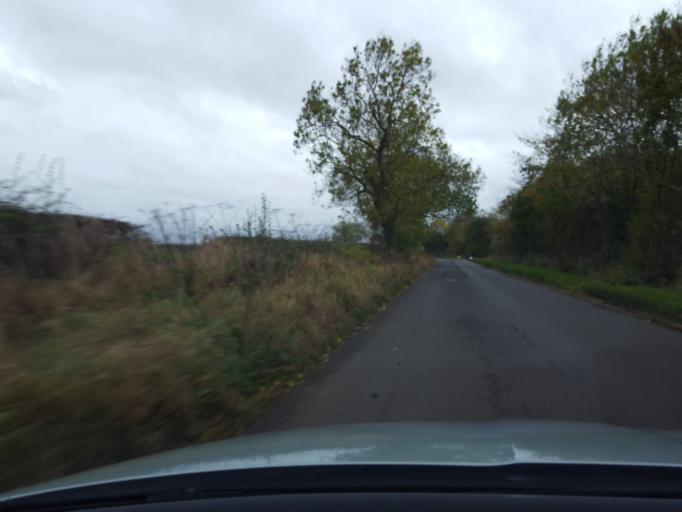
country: GB
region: Scotland
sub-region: West Lothian
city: Kirknewton
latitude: 55.9116
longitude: -3.4341
